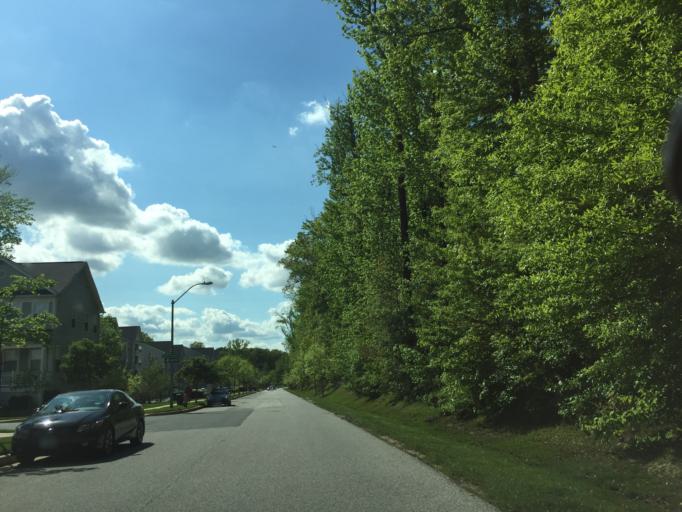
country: US
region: Maryland
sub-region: Baltimore County
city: Middle River
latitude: 39.3172
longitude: -76.4412
